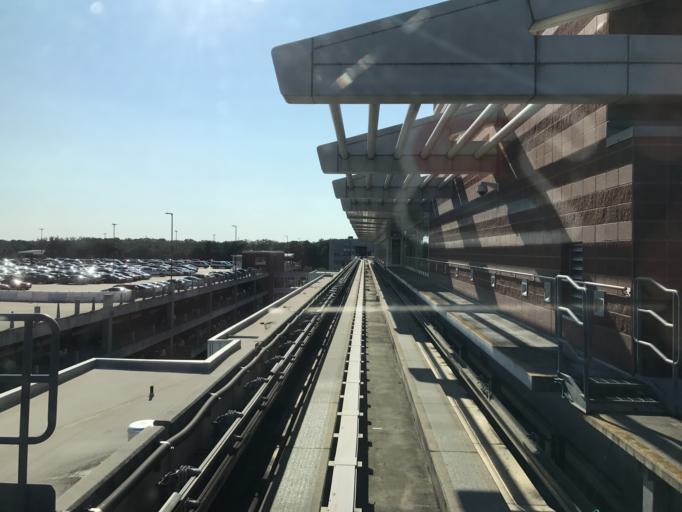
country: US
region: Georgia
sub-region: Fulton County
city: College Park
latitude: 33.6398
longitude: -84.4635
